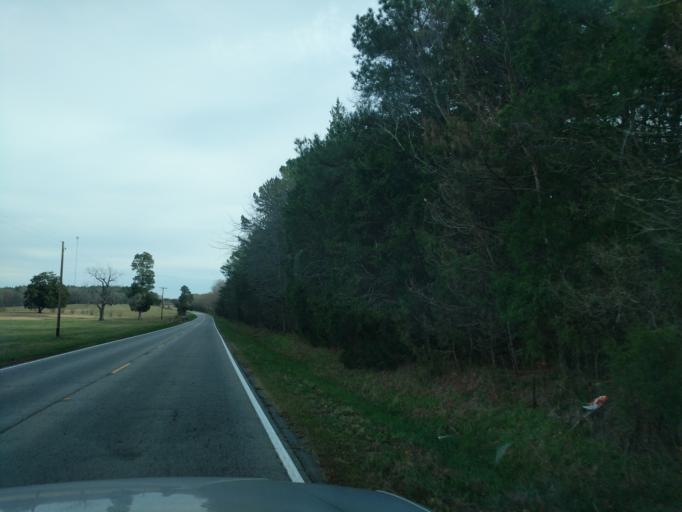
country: US
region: South Carolina
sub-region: Pickens County
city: Liberty
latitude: 34.7072
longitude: -82.6568
